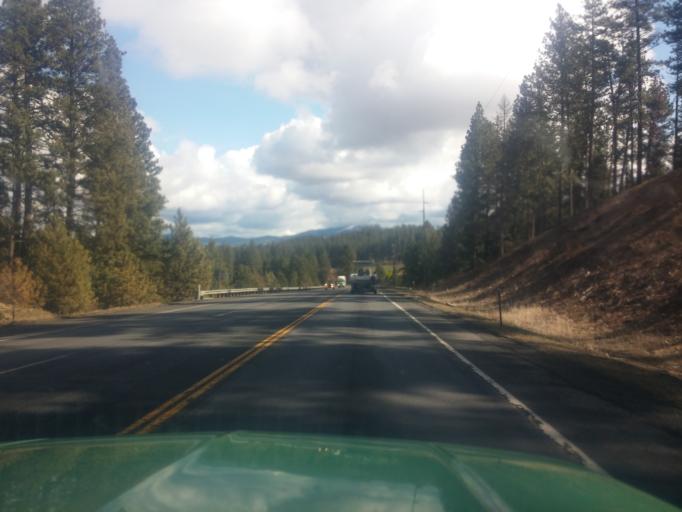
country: US
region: Idaho
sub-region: Latah County
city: Moscow
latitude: 46.9093
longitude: -116.9580
